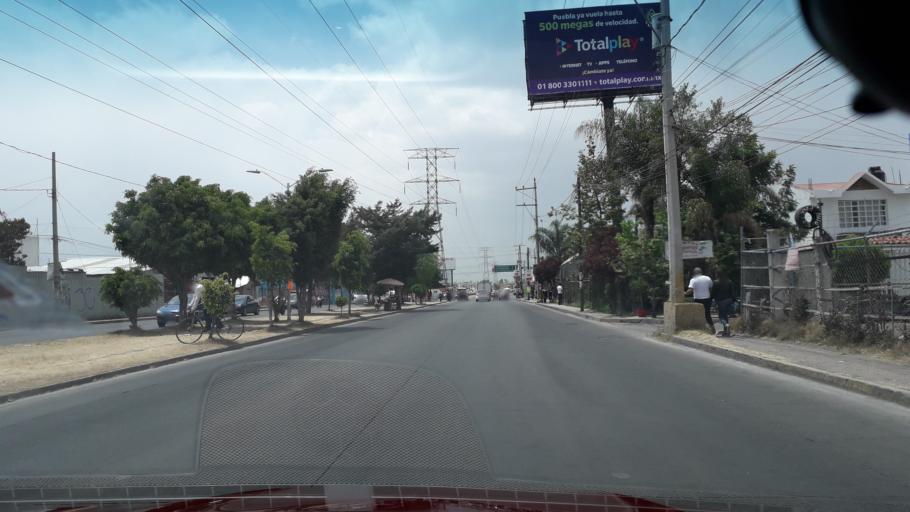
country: MX
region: Puebla
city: Puebla
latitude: 19.0046
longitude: -98.2369
